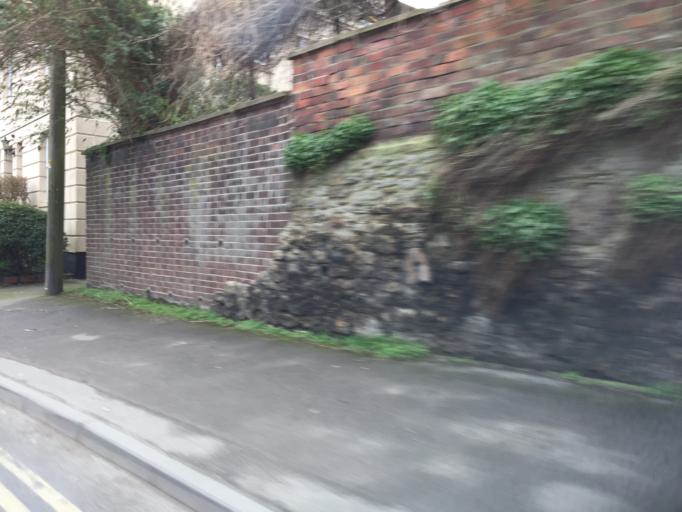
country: GB
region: England
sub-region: Oxfordshire
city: Wantage
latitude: 51.5883
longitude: -1.4231
